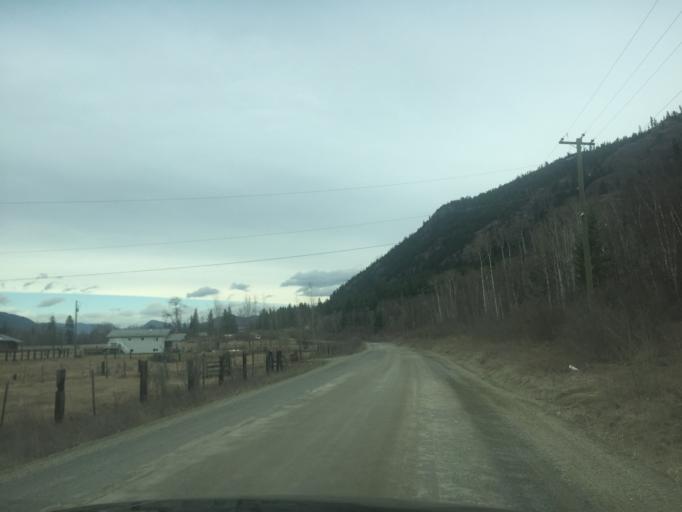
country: CA
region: British Columbia
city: Kamloops
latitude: 51.2661
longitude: -120.1523
